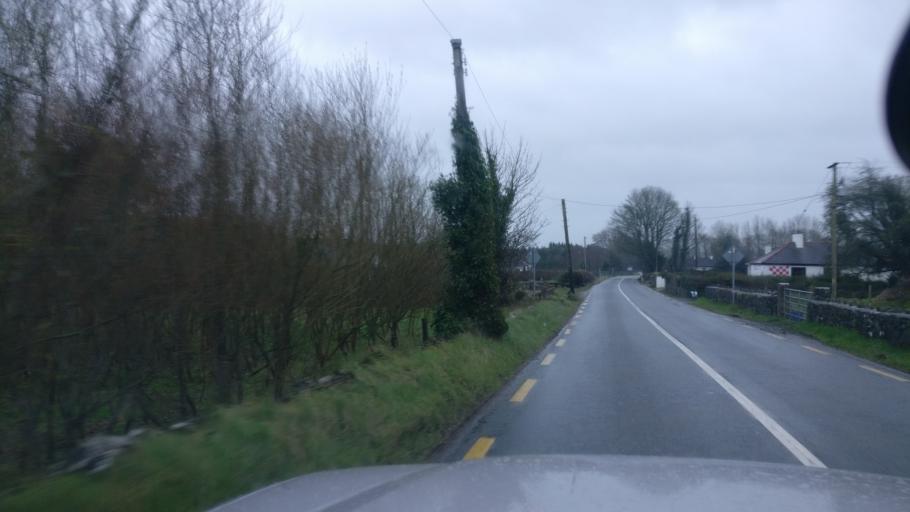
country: IE
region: Connaught
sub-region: County Galway
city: Ballinasloe
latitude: 53.2448
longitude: -8.1740
